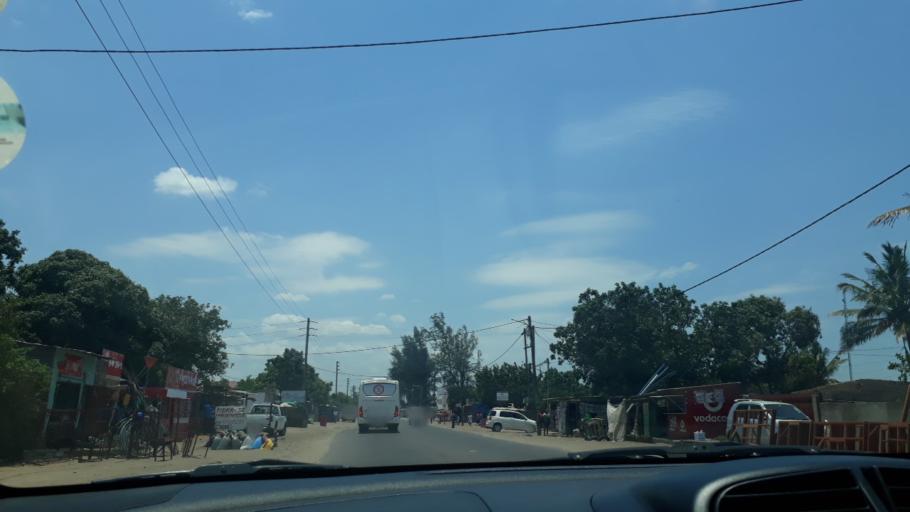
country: MZ
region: Maputo City
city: Maputo
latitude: -25.8949
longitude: 32.6011
